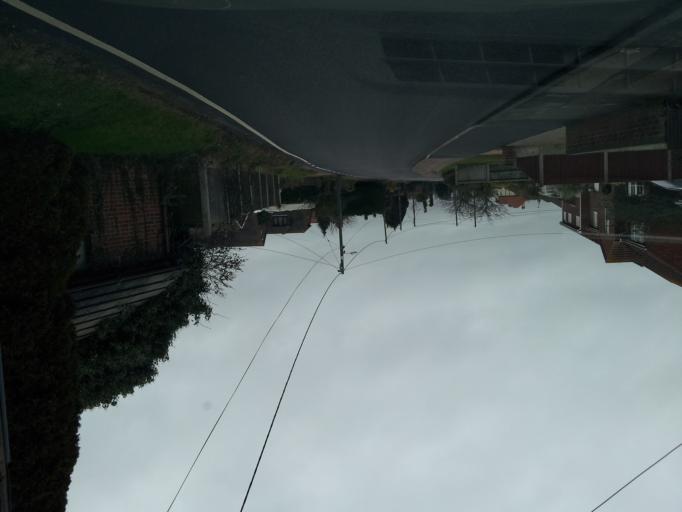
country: GB
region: England
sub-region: Essex
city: Dovercourt
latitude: 51.9236
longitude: 1.2304
